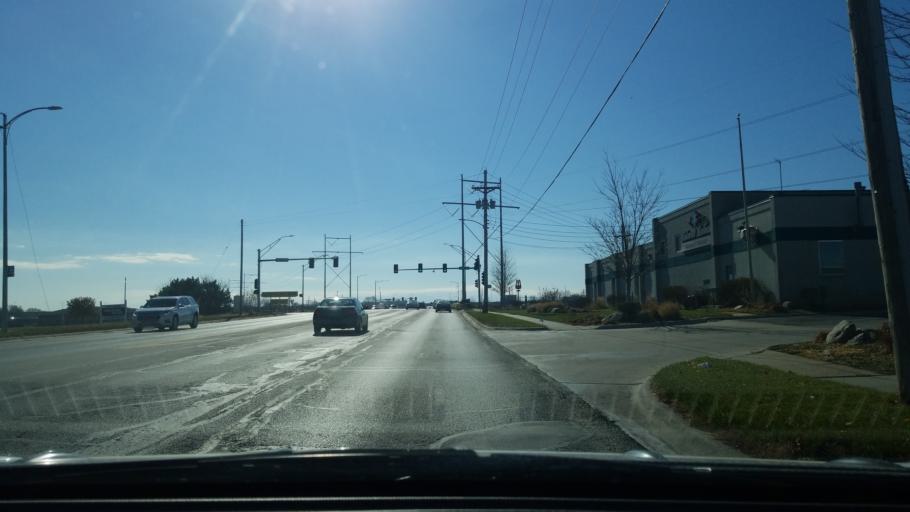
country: US
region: Nebraska
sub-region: Douglas County
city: Ralston
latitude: 41.2285
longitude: -96.0432
